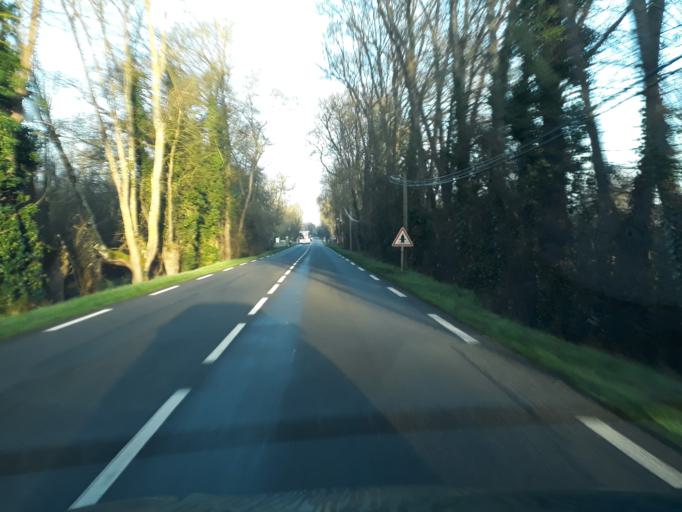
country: FR
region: Midi-Pyrenees
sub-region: Departement de la Haute-Garonne
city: Longages
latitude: 43.3581
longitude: 1.2132
